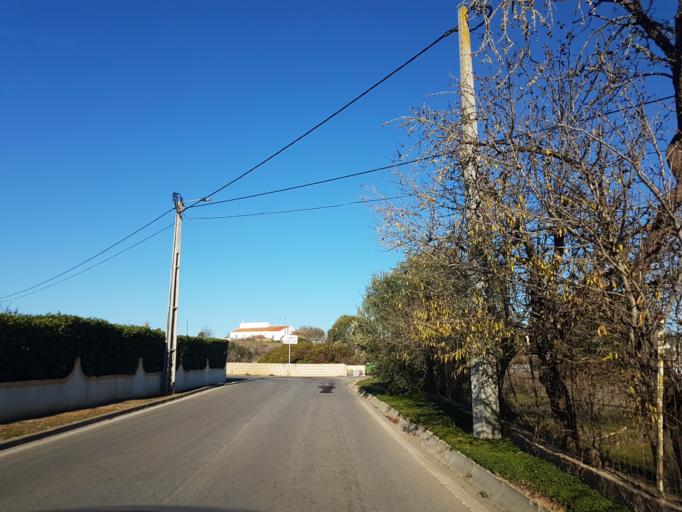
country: PT
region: Faro
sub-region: Lagoa
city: Lagoa
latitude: 37.1170
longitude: -8.4126
